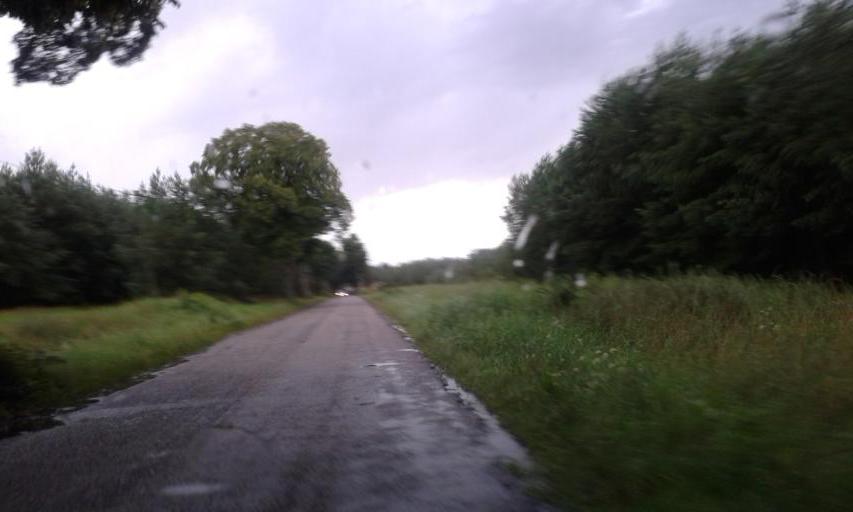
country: PL
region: Greater Poland Voivodeship
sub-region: Powiat zlotowski
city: Sypniewo
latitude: 53.4735
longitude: 16.5162
